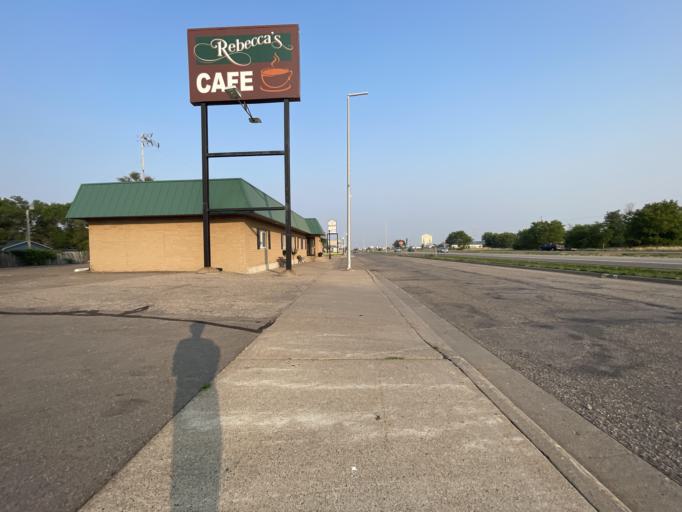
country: US
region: Minnesota
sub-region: Sherburne County
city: Becker
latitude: 45.3923
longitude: -93.8756
